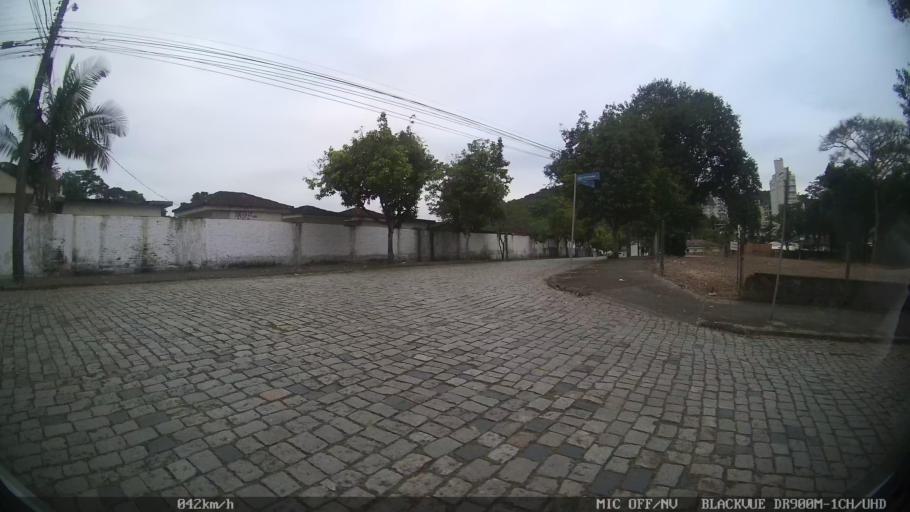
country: BR
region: Santa Catarina
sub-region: Joinville
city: Joinville
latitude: -26.3096
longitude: -48.8592
